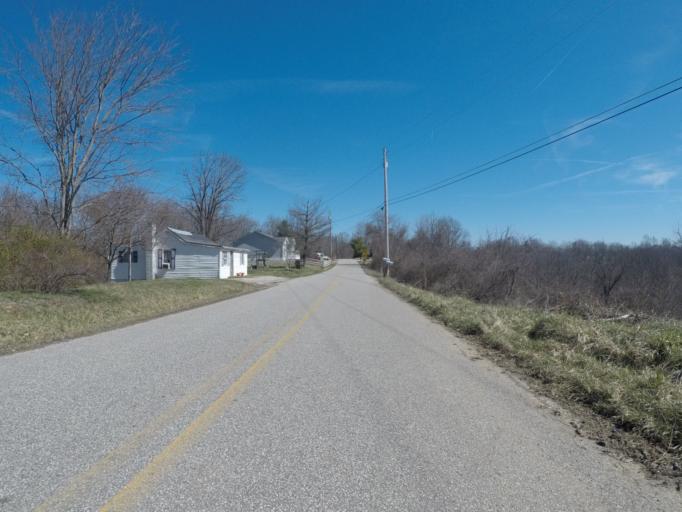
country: US
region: West Virginia
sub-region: Cabell County
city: Huntington
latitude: 38.4504
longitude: -82.4912
